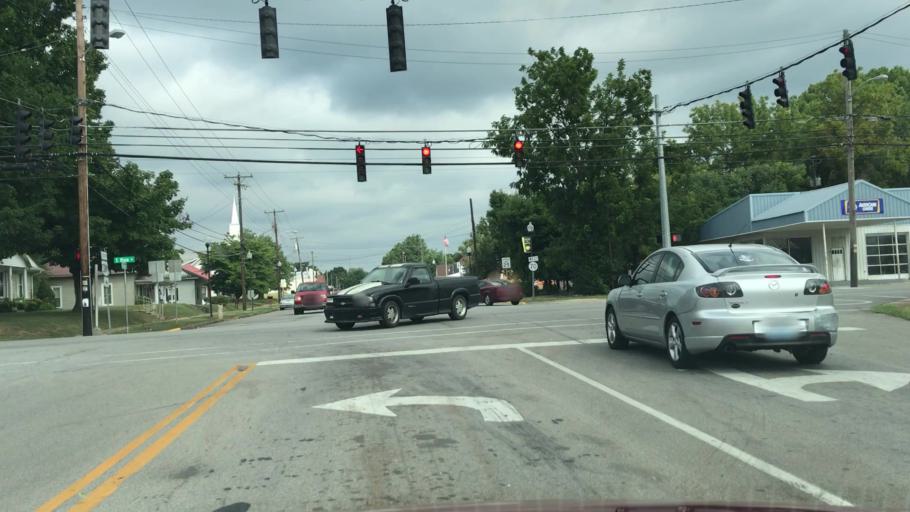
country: US
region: Kentucky
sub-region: Barren County
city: Cave City
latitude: 37.1356
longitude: -85.9557
